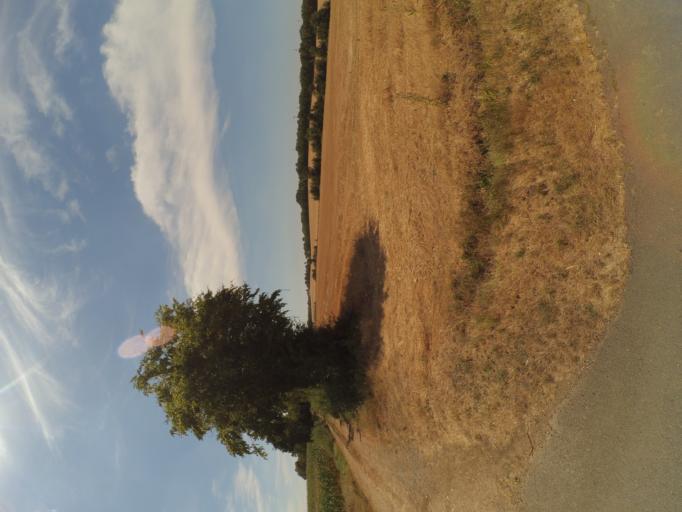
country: FR
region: Poitou-Charentes
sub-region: Departement de la Vienne
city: Usson-du-Poitou
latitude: 46.3189
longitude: 0.4892
